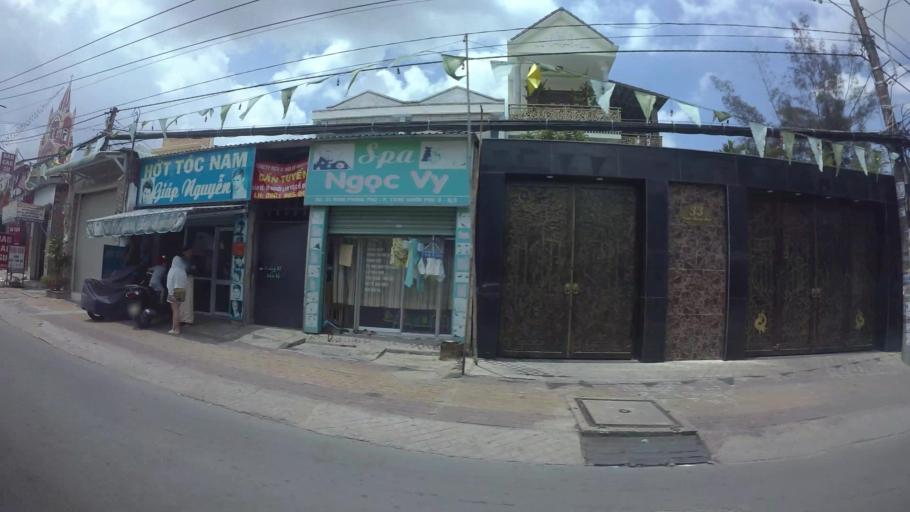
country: VN
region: Ho Chi Minh City
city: Quan Chin
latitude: 10.8403
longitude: 106.7811
